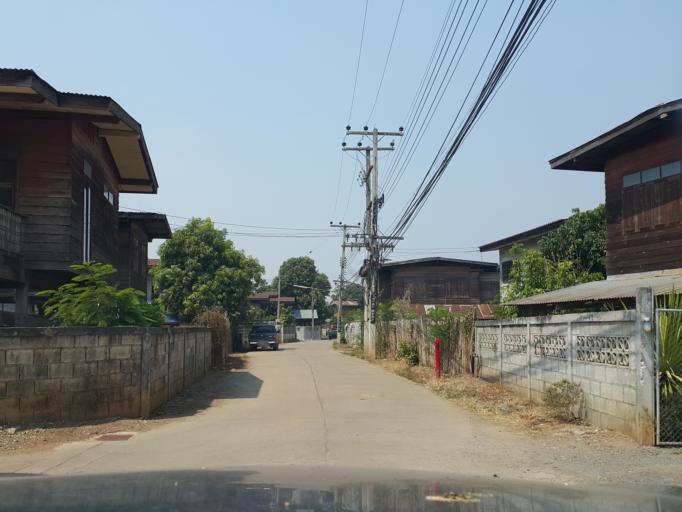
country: TH
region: Sukhothai
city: Thung Saliam
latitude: 17.3136
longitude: 99.5562
